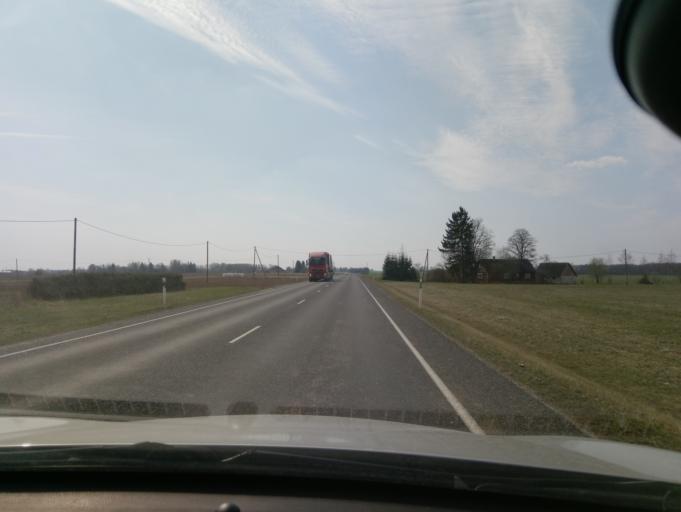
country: EE
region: Viljandimaa
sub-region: Vohma linn
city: Vohma
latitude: 58.6862
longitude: 25.6196
